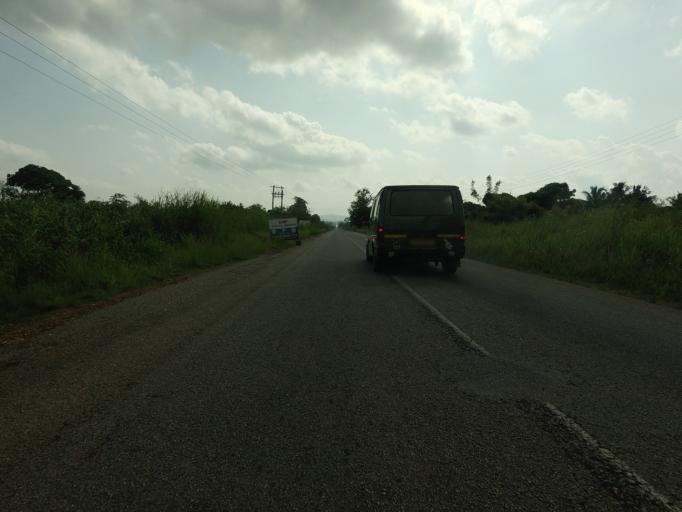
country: GH
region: Volta
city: Ho
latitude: 6.5936
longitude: 0.5421
